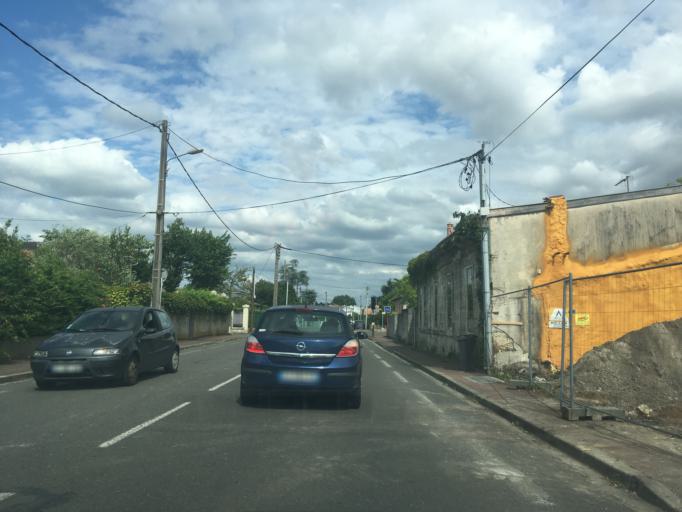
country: FR
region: Aquitaine
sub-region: Departement de la Gironde
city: Merignac
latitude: 44.8525
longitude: -0.6440
